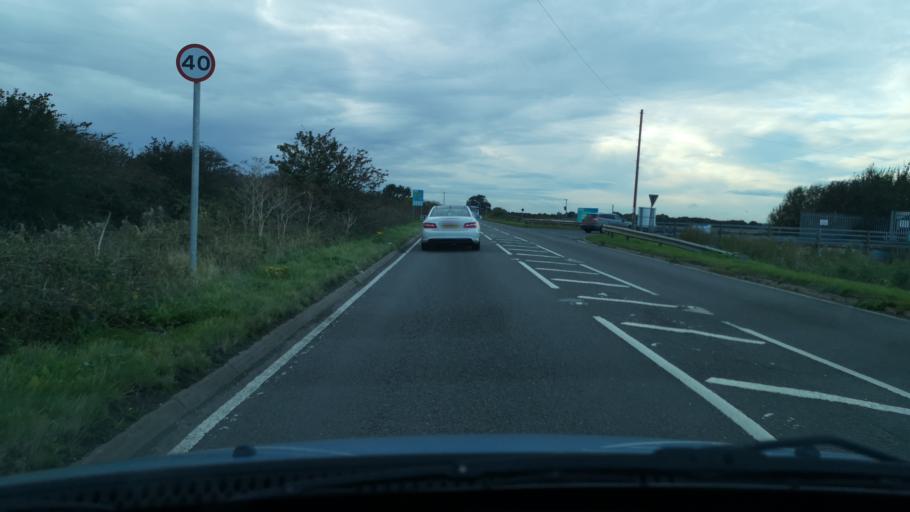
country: GB
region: England
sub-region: North Lincolnshire
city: Belton
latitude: 53.5805
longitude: -0.7874
